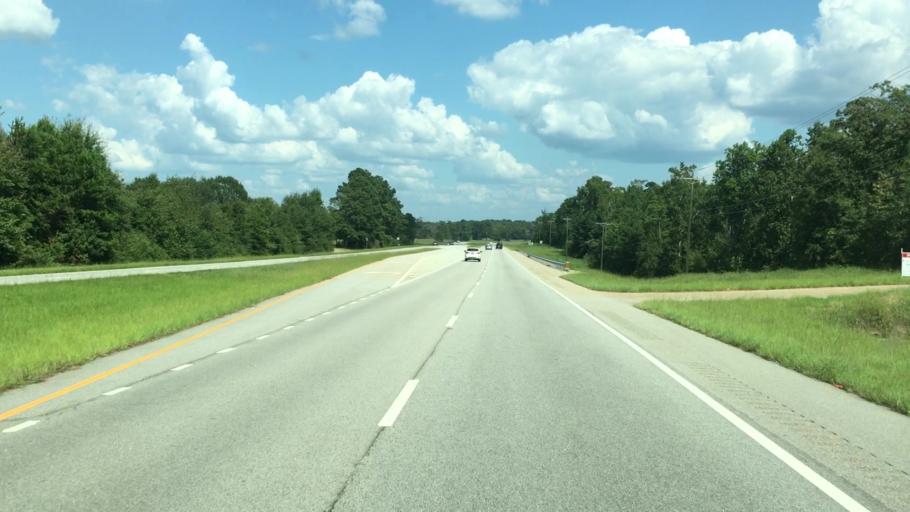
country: US
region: Georgia
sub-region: Putnam County
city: Eatonton
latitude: 33.2729
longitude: -83.3578
